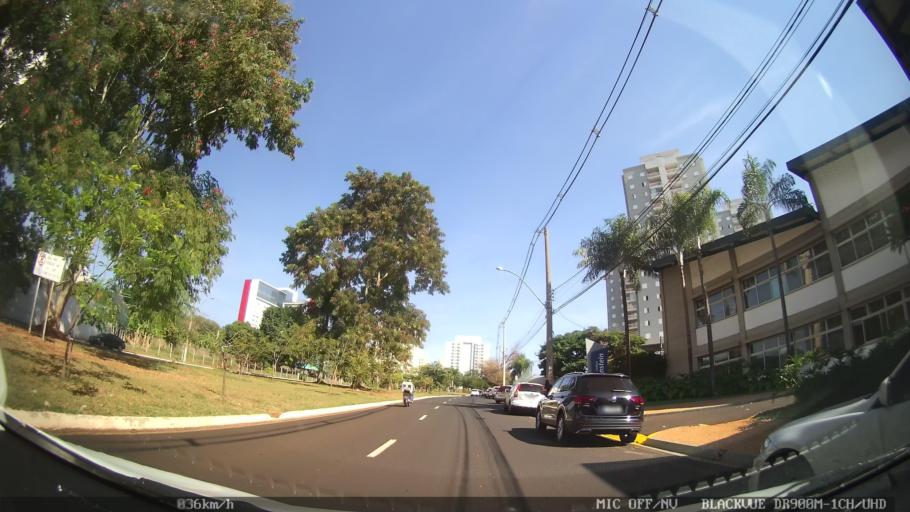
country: BR
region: Sao Paulo
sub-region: Ribeirao Preto
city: Ribeirao Preto
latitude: -21.2140
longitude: -47.8206
